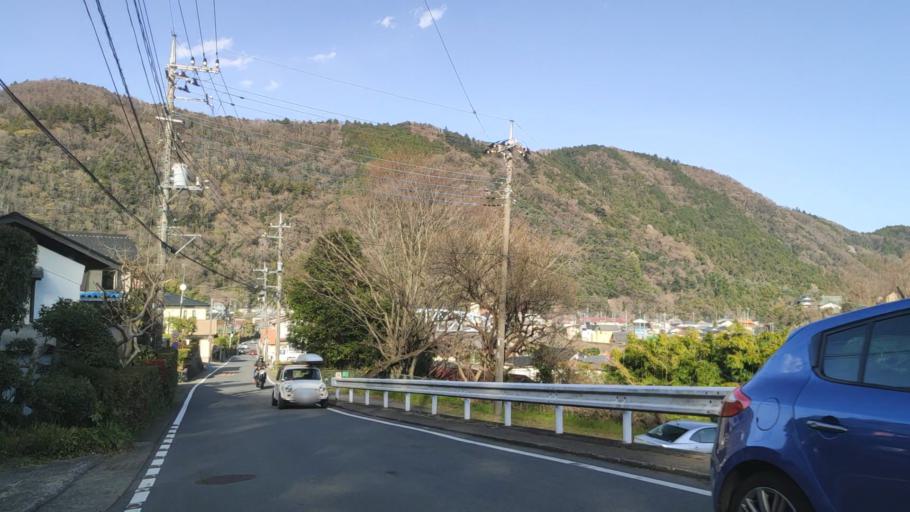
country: JP
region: Tokyo
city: Hachioji
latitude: 35.5443
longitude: 139.2620
